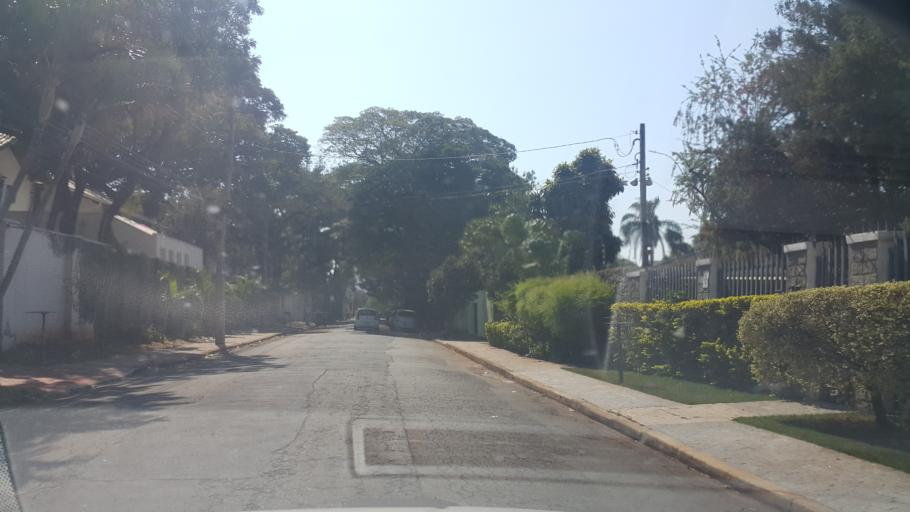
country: BR
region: Sao Paulo
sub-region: Campinas
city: Campinas
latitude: -22.8622
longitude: -47.0515
